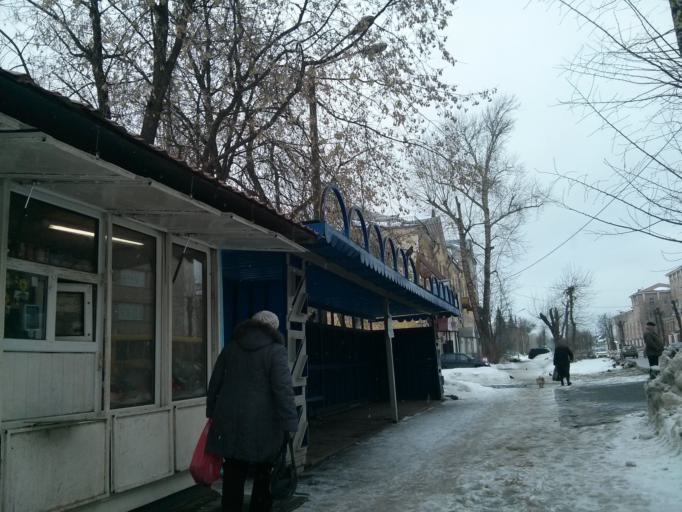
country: RU
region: Vladimir
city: Murom
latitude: 55.5552
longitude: 42.0610
